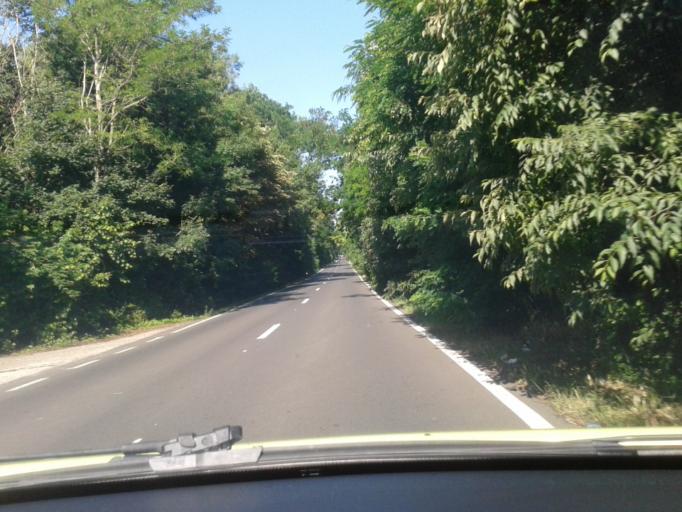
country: RO
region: Constanta
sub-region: Comuna Douazeci si Trei August
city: Douazeci si Trei August
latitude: 43.8749
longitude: 28.5823
